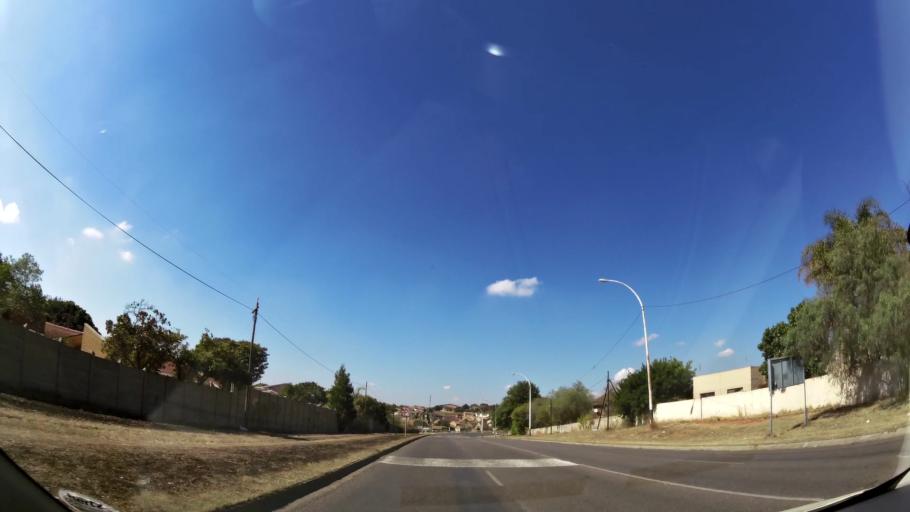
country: ZA
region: Mpumalanga
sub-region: Nkangala District Municipality
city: Witbank
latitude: -25.8621
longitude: 29.2389
